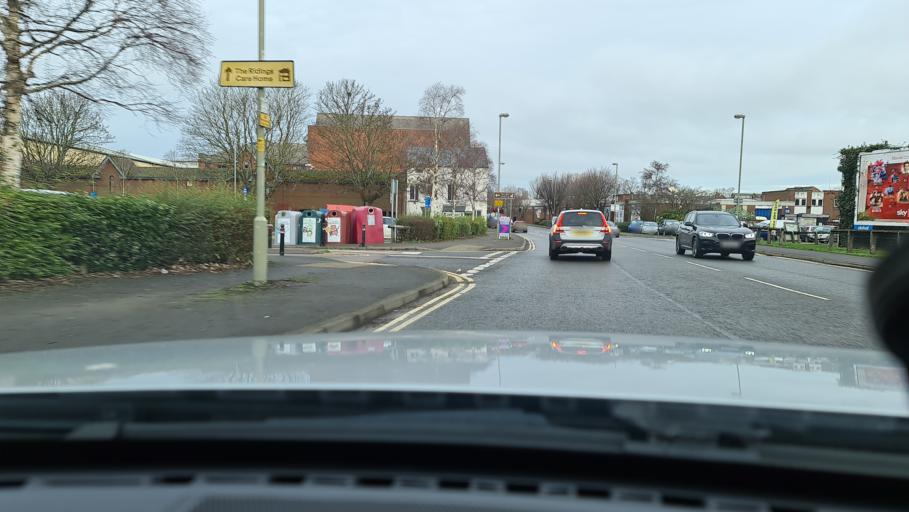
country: GB
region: England
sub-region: Oxfordshire
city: Banbury
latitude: 52.0588
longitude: -1.3323
